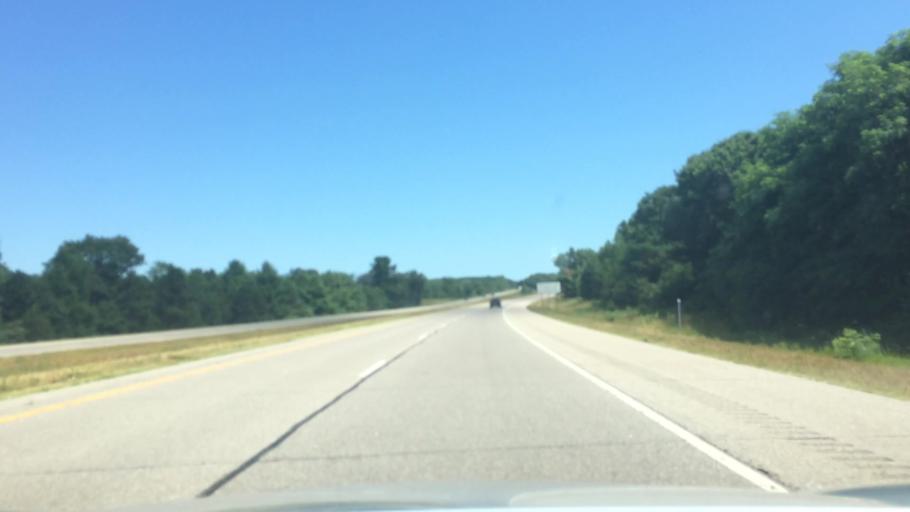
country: US
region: Wisconsin
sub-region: Marquette County
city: Westfield
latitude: 44.0632
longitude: -89.5415
